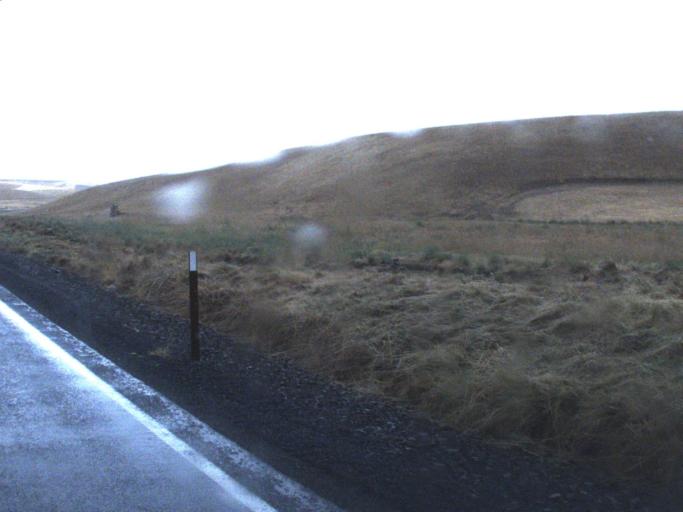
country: US
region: Washington
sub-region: Spokane County
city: Cheney
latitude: 47.1913
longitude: -117.8740
